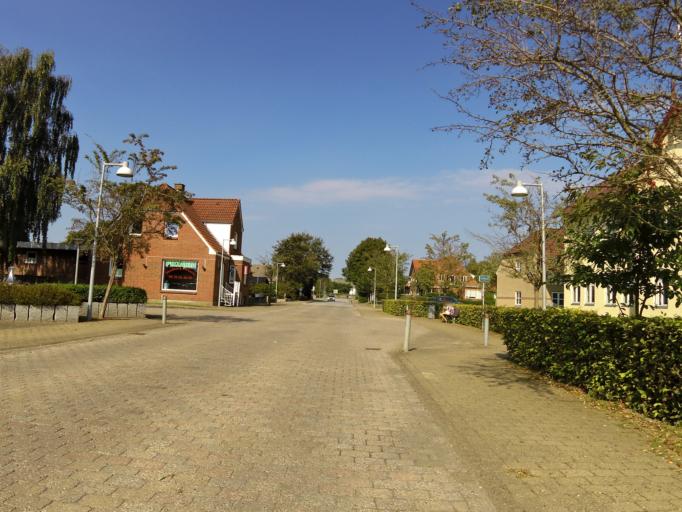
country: DK
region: South Denmark
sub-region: Vejen Kommune
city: Vejen
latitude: 55.4202
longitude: 9.1532
